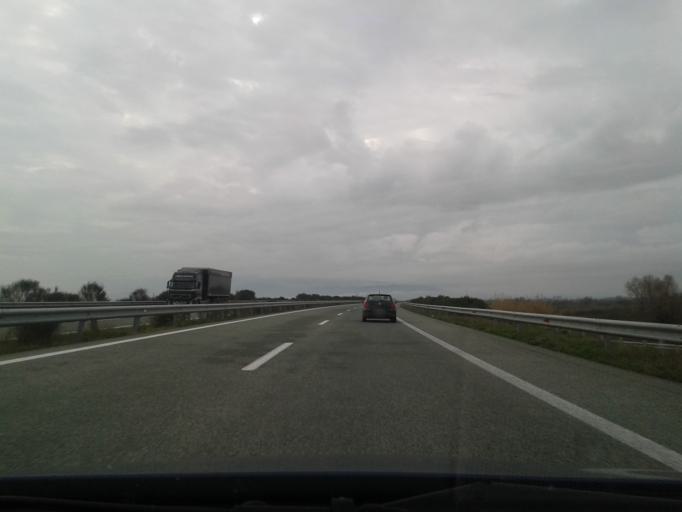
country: GR
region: West Greece
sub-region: Nomos Aitolias kai Akarnanias
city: Lepenou
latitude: 38.6611
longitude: 21.2413
